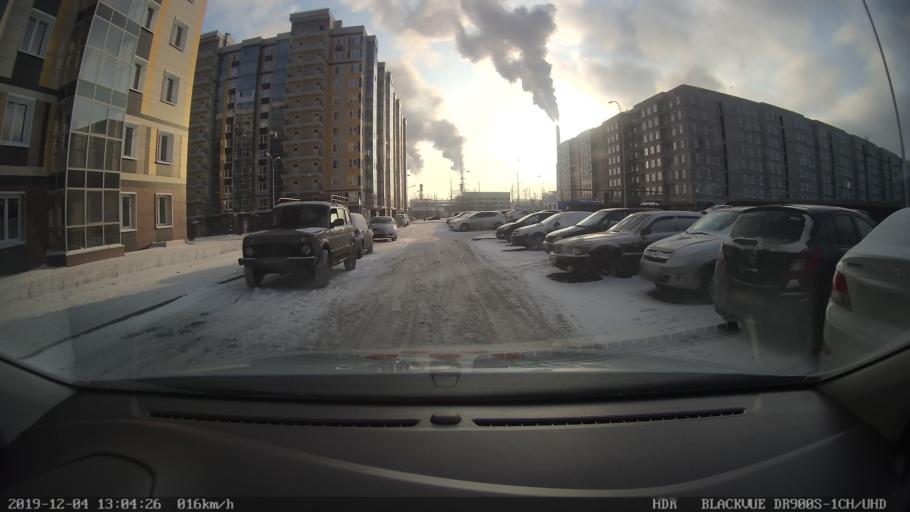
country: RU
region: Tatarstan
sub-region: Gorod Kazan'
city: Kazan
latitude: 55.8521
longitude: 49.0647
